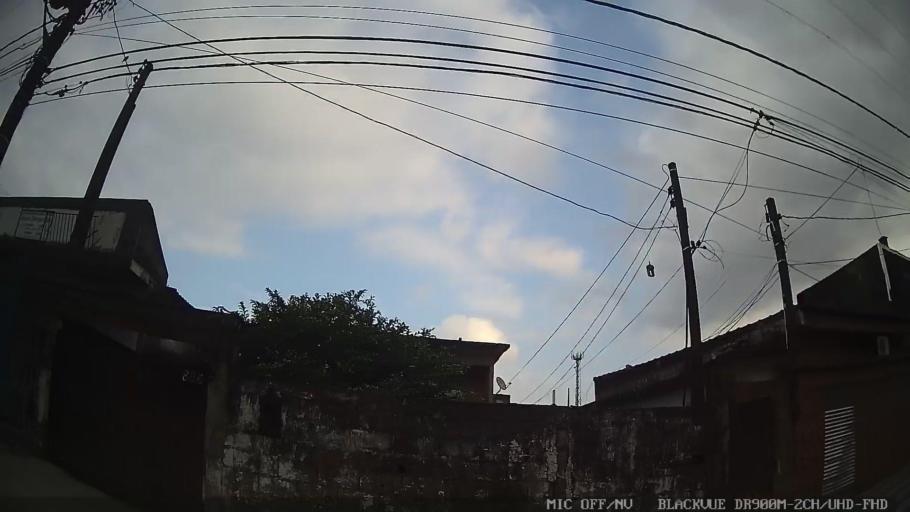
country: BR
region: Sao Paulo
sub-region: Santos
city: Santos
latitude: -23.9503
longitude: -46.2864
